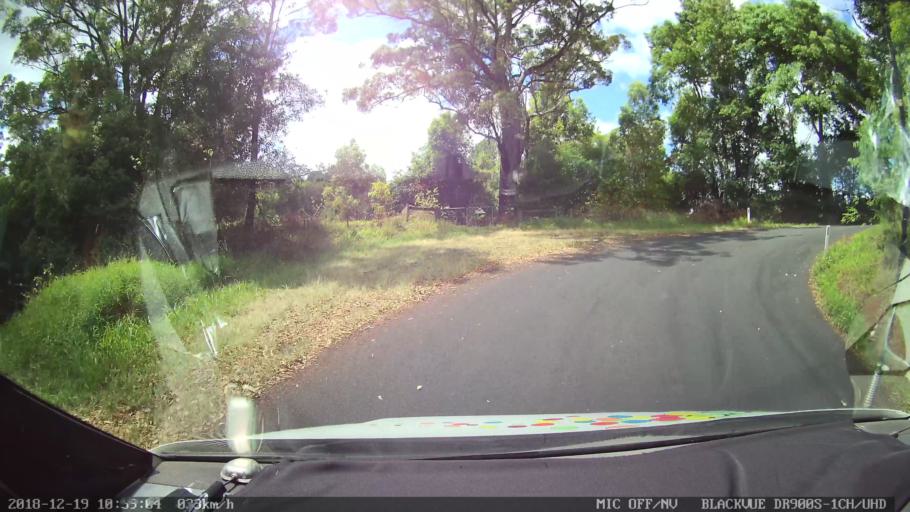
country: AU
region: New South Wales
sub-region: Lismore Municipality
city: Nimbin
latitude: -28.5956
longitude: 153.2639
